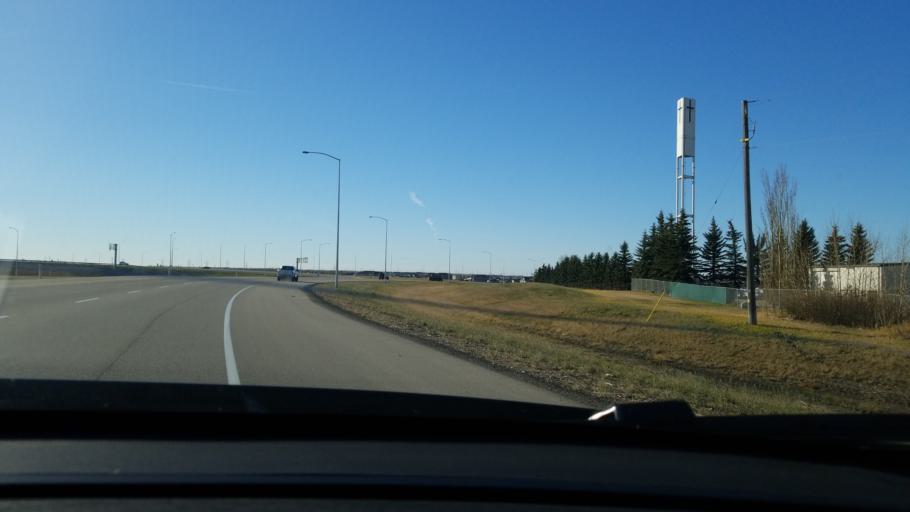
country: CA
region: Alberta
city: Sherwood Park
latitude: 53.4865
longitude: -113.3440
